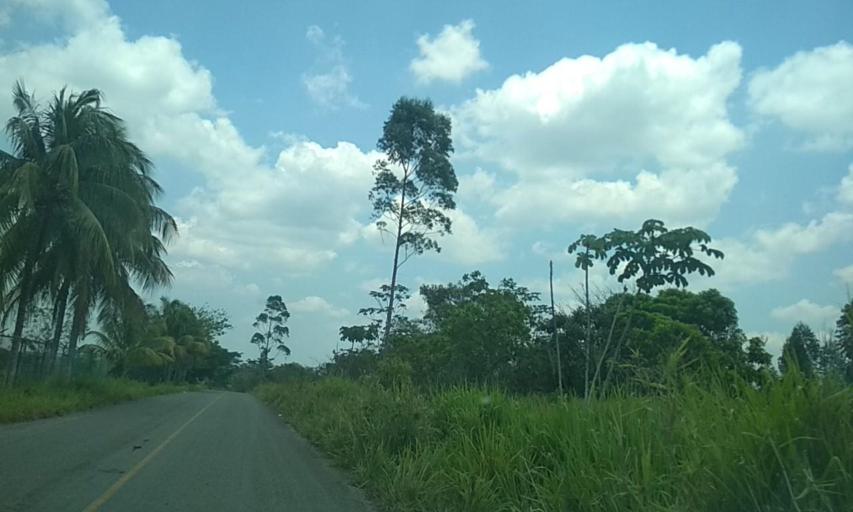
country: MX
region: Tabasco
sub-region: Huimanguillo
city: Francisco Rueda
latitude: 17.7917
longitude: -93.8466
